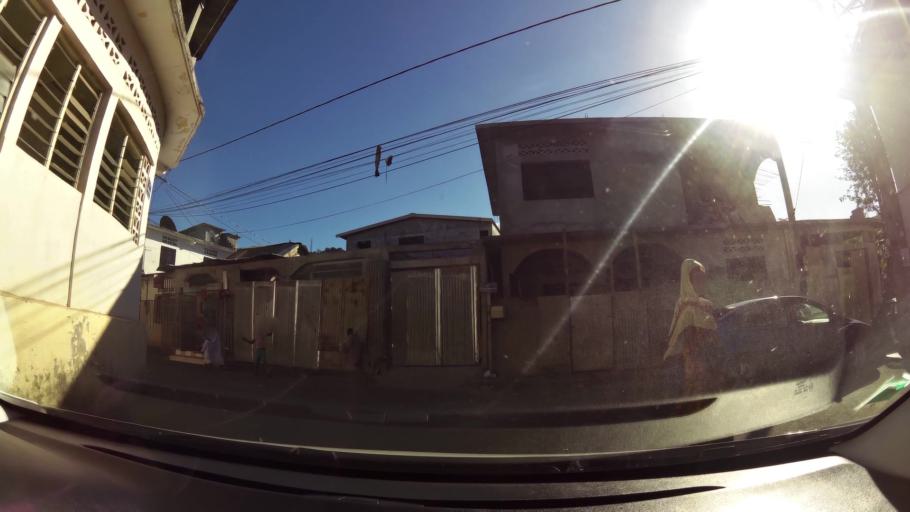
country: YT
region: Mamoudzou
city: Mamoudzou
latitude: -12.7718
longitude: 45.2203
